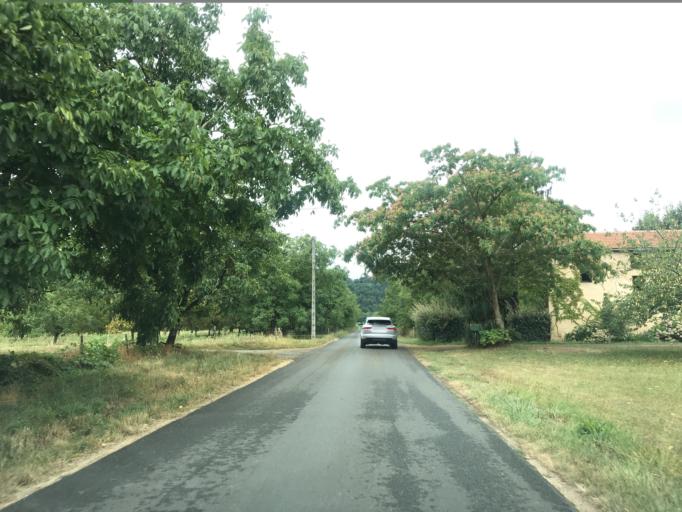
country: FR
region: Aquitaine
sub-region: Departement de la Dordogne
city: Domme
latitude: 44.8154
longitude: 1.2243
